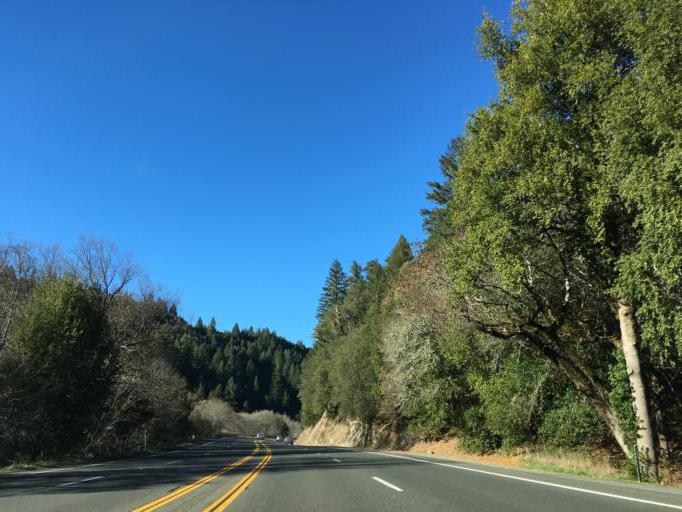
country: US
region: California
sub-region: Mendocino County
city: Brooktrails
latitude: 39.5274
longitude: -123.4015
